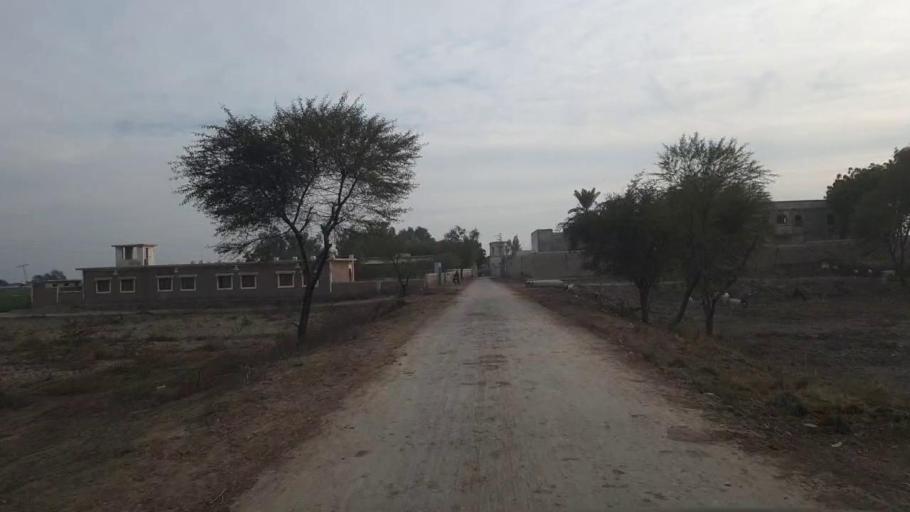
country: PK
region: Sindh
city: Shahpur Chakar
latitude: 26.1332
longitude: 68.6072
